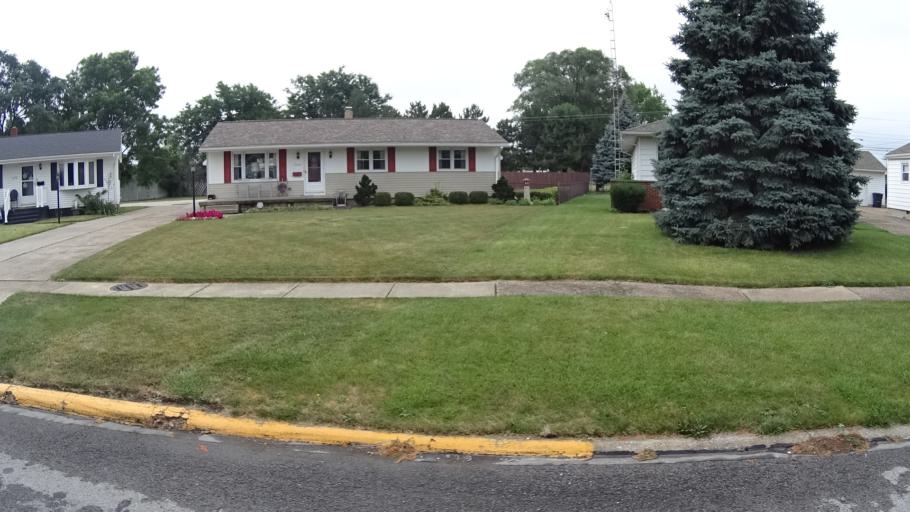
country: US
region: Ohio
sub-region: Erie County
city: Sandusky
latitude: 41.4443
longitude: -82.6851
